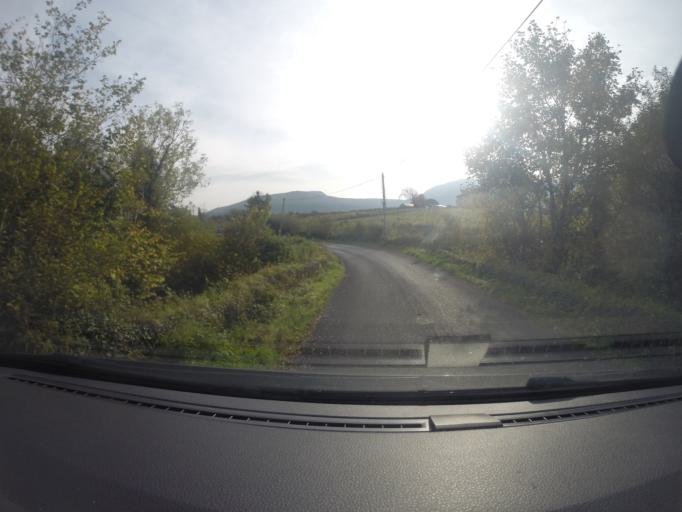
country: IE
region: Connaught
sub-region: County Leitrim
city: Kinlough
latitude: 54.3307
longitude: -8.3468
